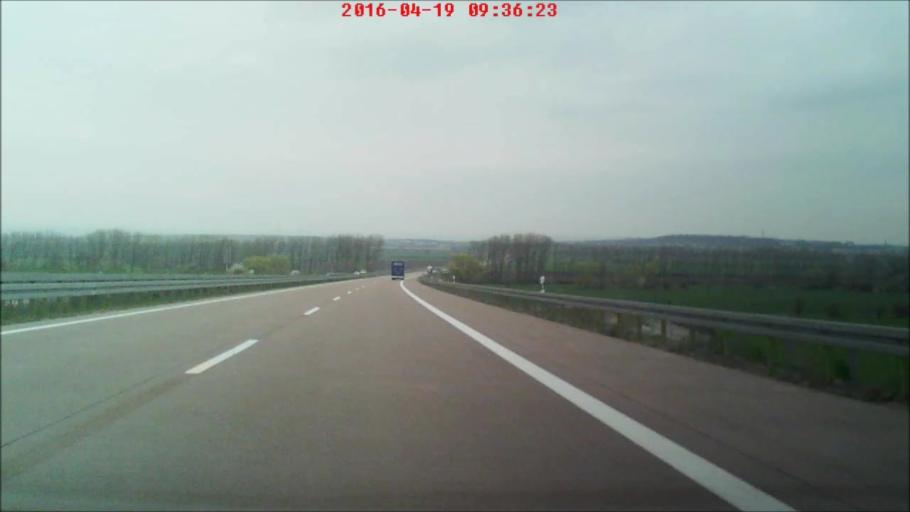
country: DE
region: Thuringia
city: Reinsdorf
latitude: 51.3347
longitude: 11.2546
